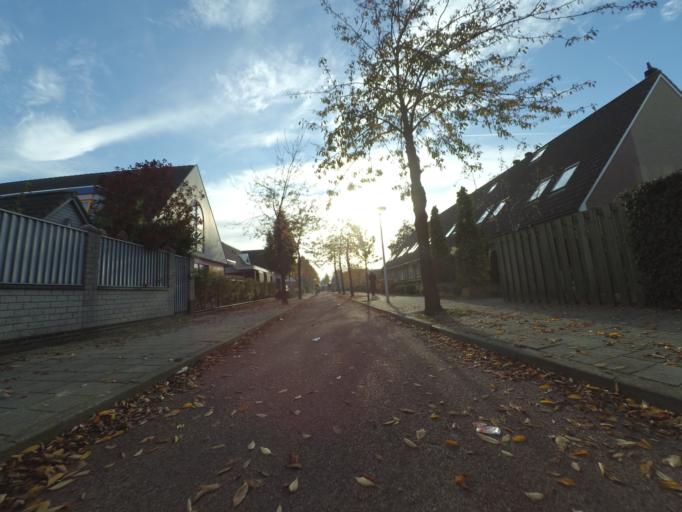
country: NL
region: Gelderland
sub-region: Gemeente Ede
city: Ede
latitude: 52.0196
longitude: 5.6542
